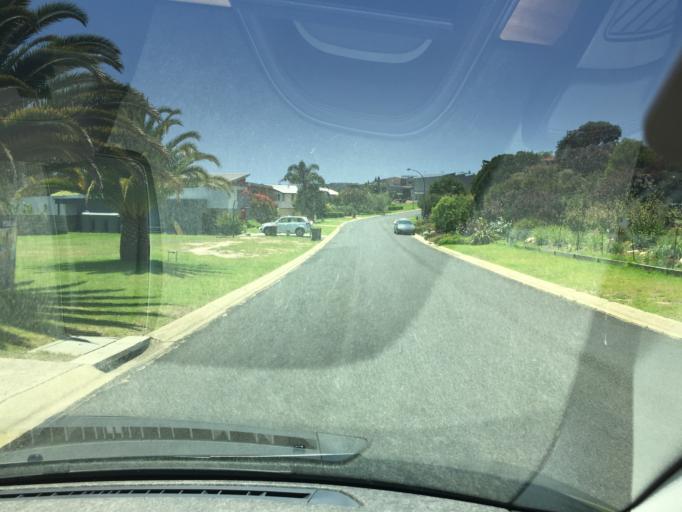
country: AU
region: New South Wales
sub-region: Bega Valley
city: Merimbula
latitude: -36.8490
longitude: 149.9319
